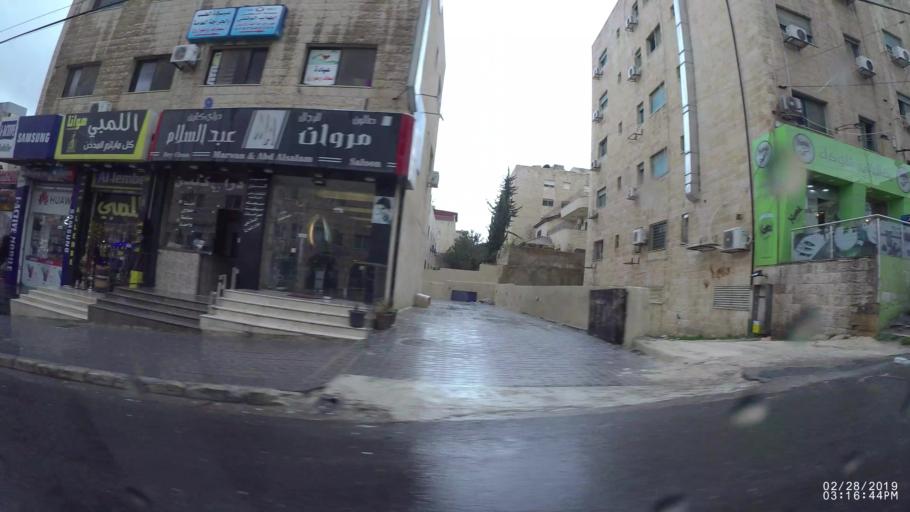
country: JO
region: Amman
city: Al Jubayhah
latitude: 32.0216
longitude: 35.8659
